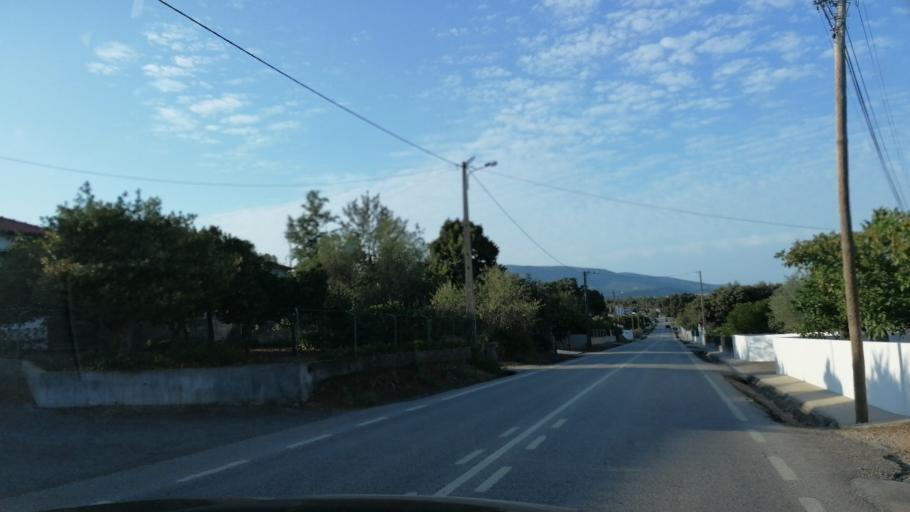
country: PT
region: Santarem
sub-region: Alcanena
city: Alcanena
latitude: 39.4463
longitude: -8.6232
